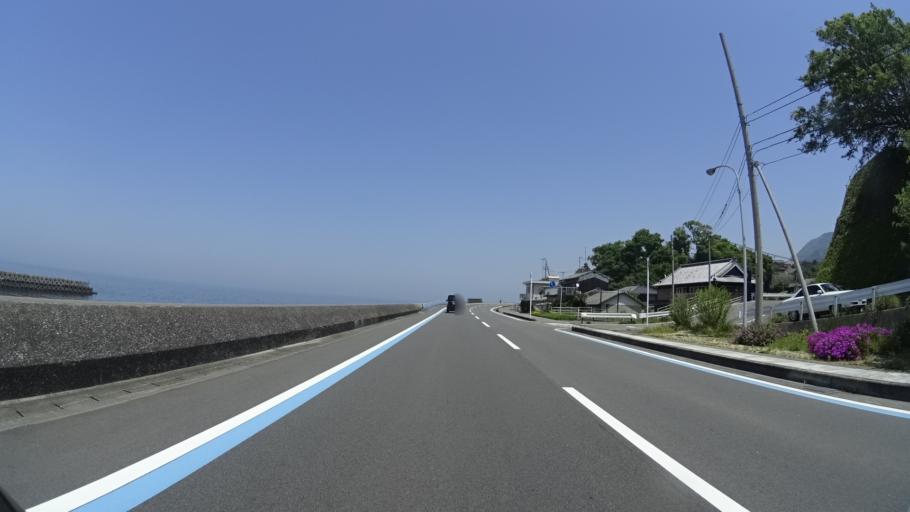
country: JP
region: Ehime
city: Iyo
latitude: 33.6818
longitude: 132.6291
